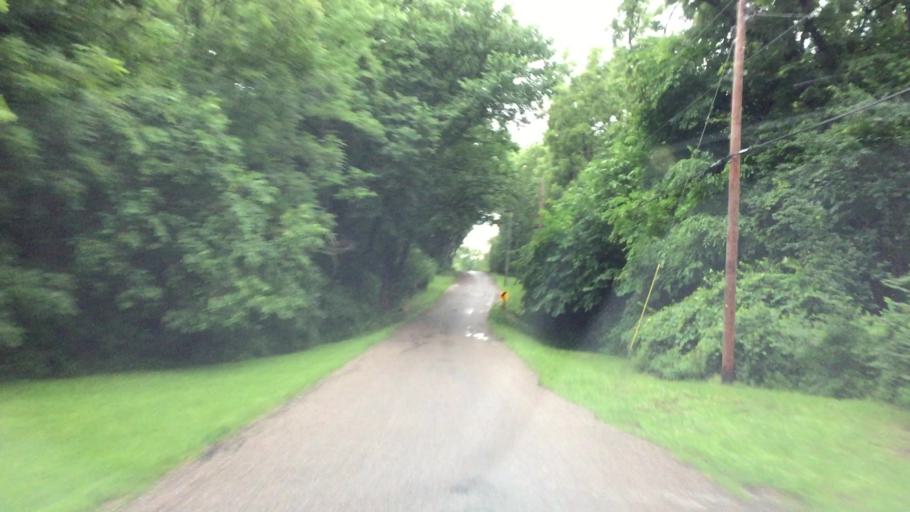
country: US
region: Illinois
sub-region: Hancock County
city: Nauvoo
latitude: 40.5363
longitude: -91.3759
